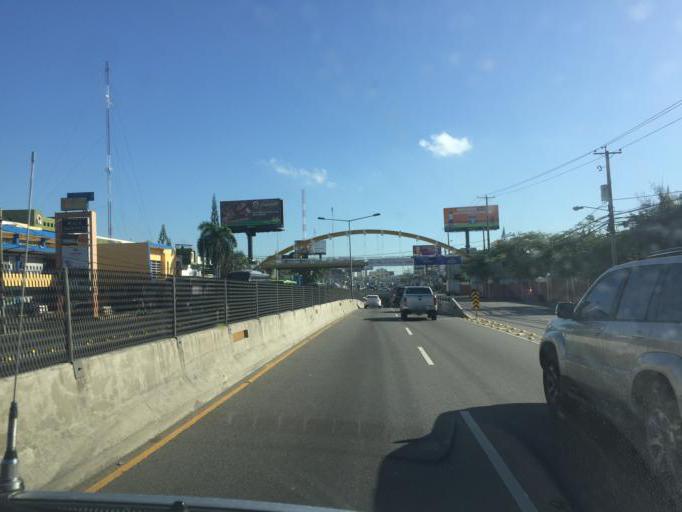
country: DO
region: Nacional
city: Bella Vista
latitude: 18.4564
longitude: -69.9515
